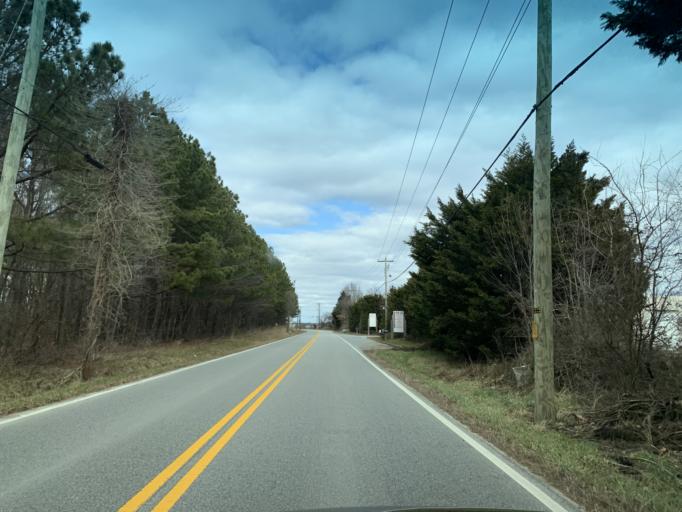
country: US
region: Maryland
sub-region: Queen Anne's County
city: Centreville
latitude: 39.0062
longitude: -76.1322
